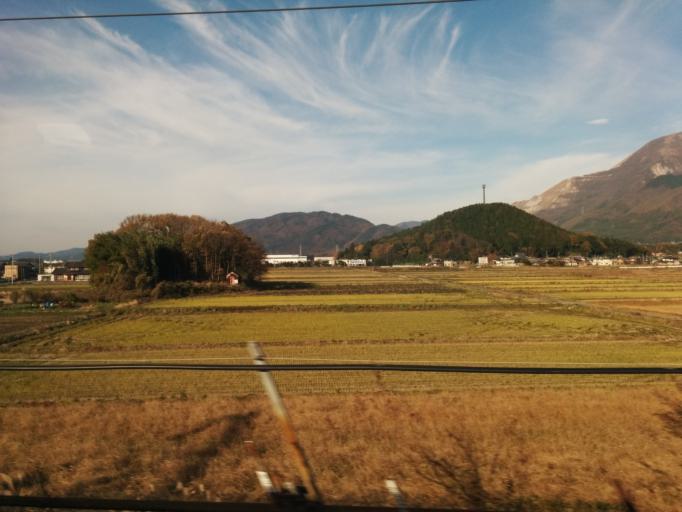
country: JP
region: Shiga Prefecture
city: Nagahama
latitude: 35.3672
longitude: 136.3704
